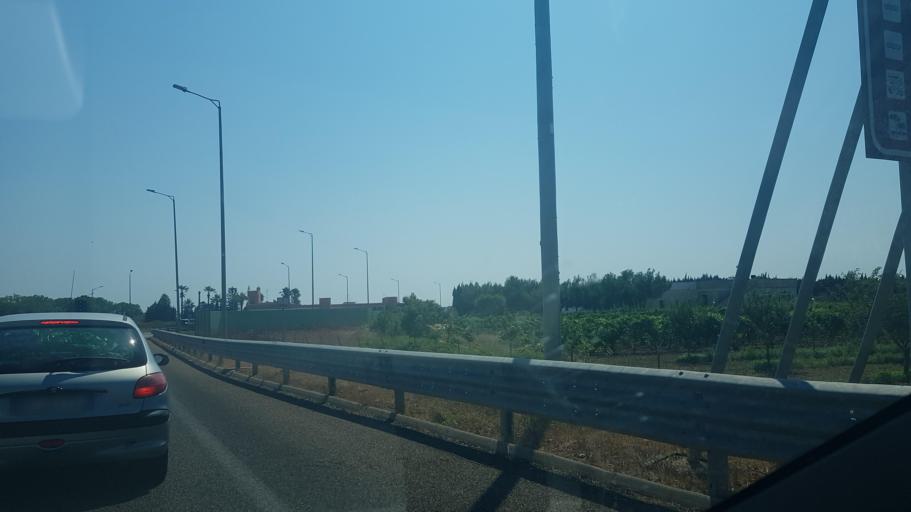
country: IT
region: Apulia
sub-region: Provincia di Lecce
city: Otranto
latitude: 40.1481
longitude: 18.4743
